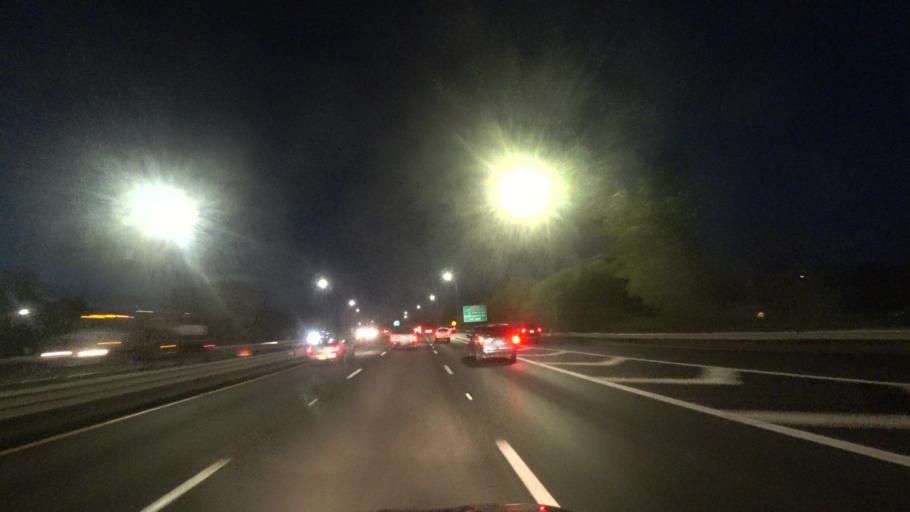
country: US
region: Massachusetts
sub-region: Essex County
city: North Andover
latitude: 42.6996
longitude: -71.1415
